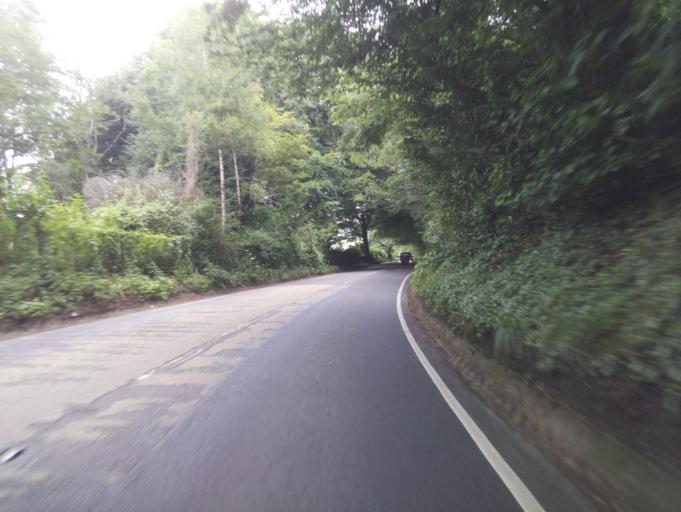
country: GB
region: England
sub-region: South Gloucestershire
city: Cold Ashton
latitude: 51.4315
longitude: -2.4023
